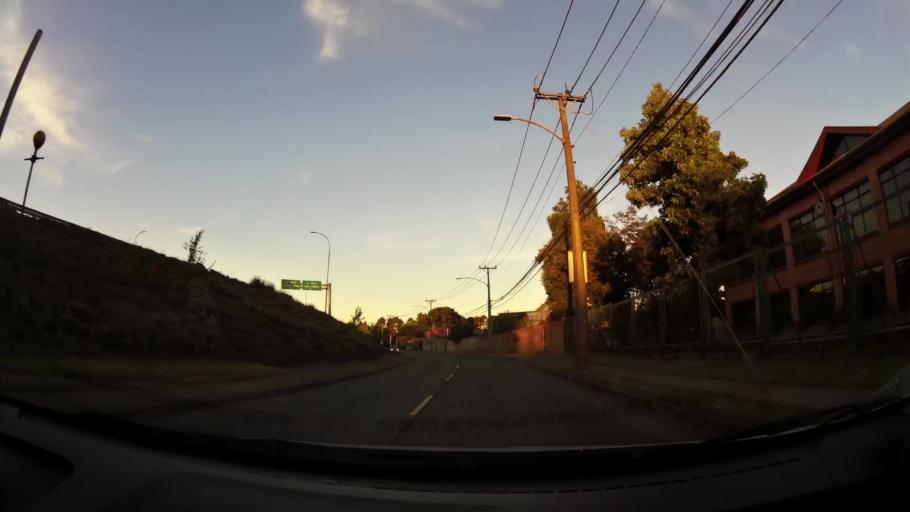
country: CL
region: Biobio
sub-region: Provincia de Concepcion
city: Concepcion
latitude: -36.8399
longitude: -73.1001
